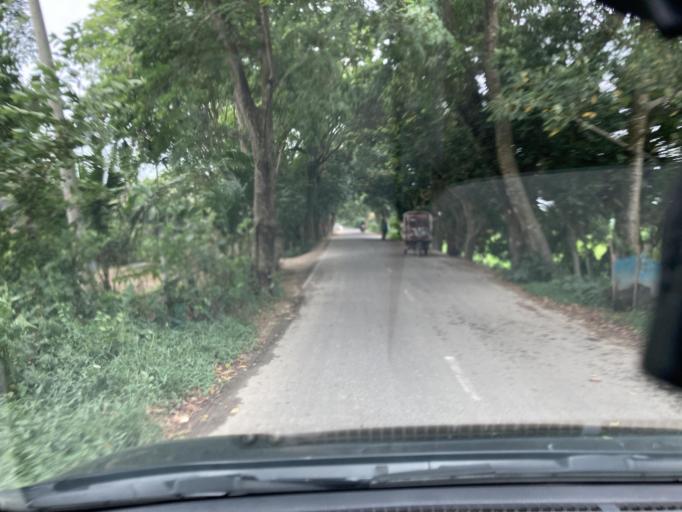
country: BD
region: Dhaka
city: Dohar
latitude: 23.7881
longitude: 90.0630
